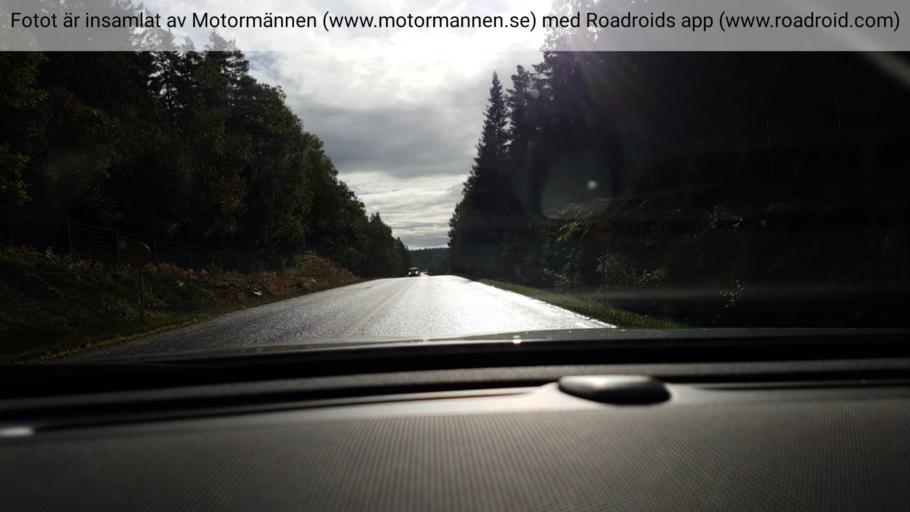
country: SE
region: Vaestra Goetaland
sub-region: Marks Kommun
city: Bua
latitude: 57.5134
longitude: 12.5694
